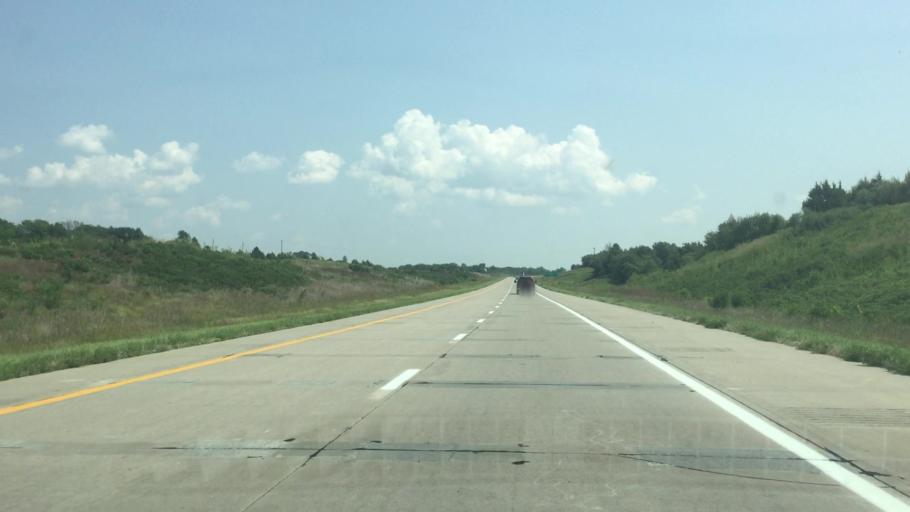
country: US
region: Kansas
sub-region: Franklin County
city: Ottawa
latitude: 38.5642
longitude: -95.3063
